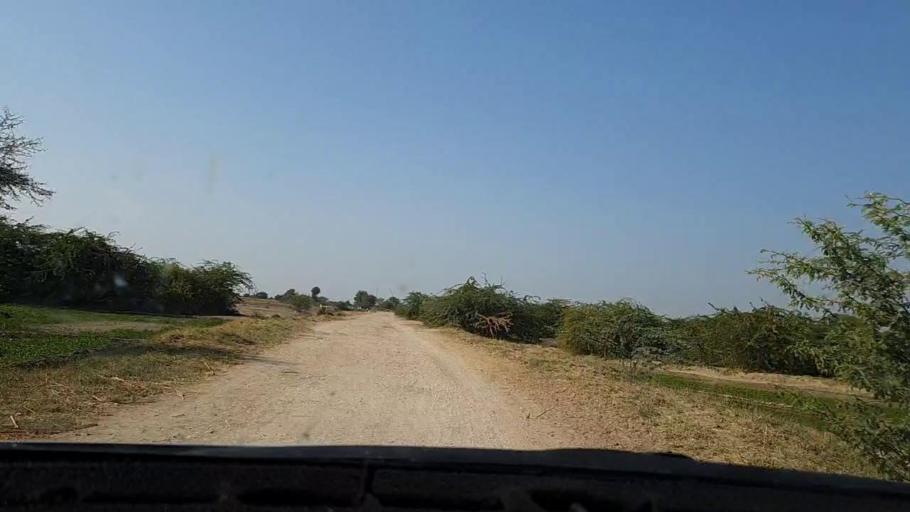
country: PK
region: Sindh
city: Tando Mittha Khan
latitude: 25.8135
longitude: 69.2909
